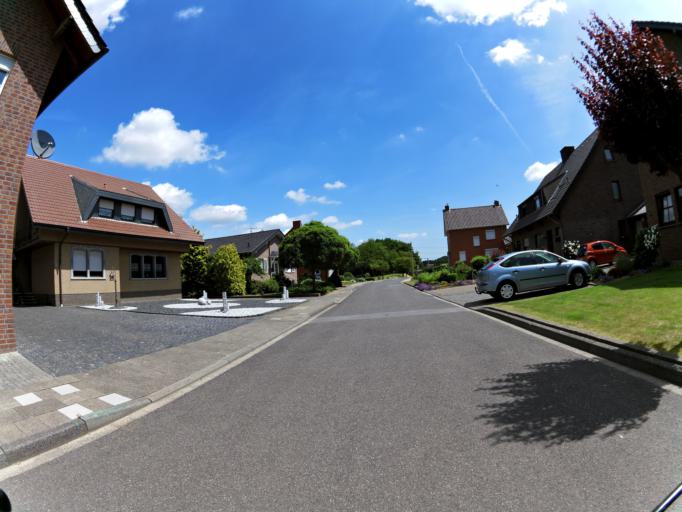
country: DE
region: North Rhine-Westphalia
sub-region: Regierungsbezirk Koln
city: Selfkant
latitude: 51.0255
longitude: 5.9418
